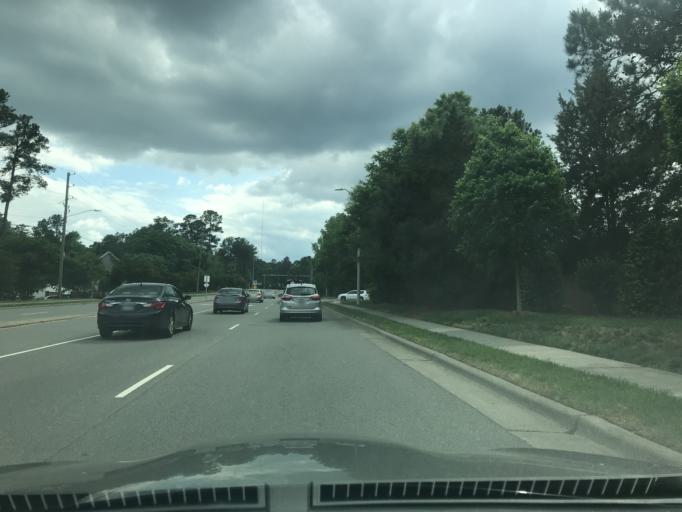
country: US
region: North Carolina
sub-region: Wake County
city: Wake Forest
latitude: 35.9310
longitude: -78.5834
